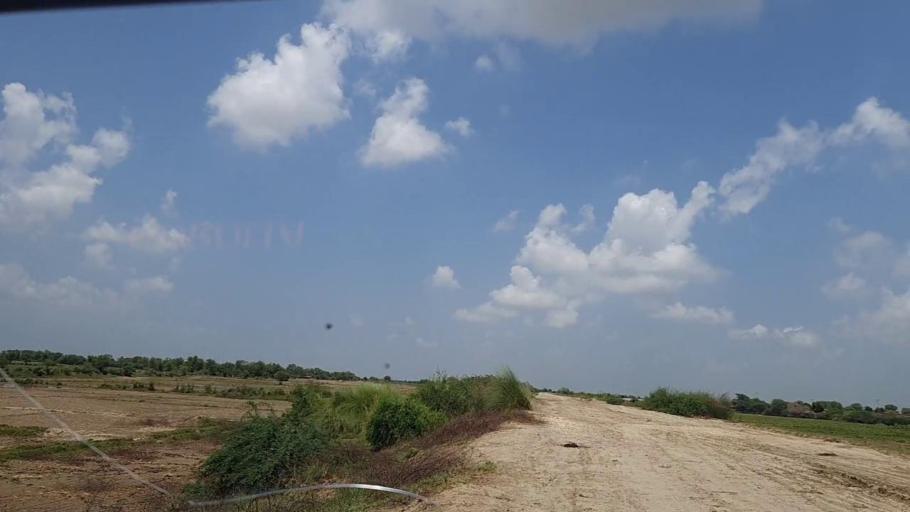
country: PK
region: Sindh
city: Tharu Shah
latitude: 26.9441
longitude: 68.0137
